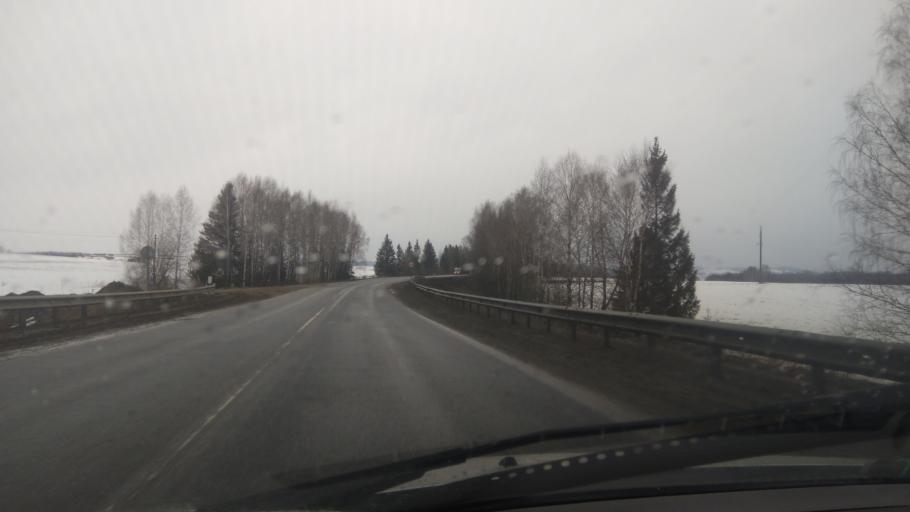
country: RU
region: Perm
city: Kukushtan
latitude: 57.4857
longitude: 56.6708
